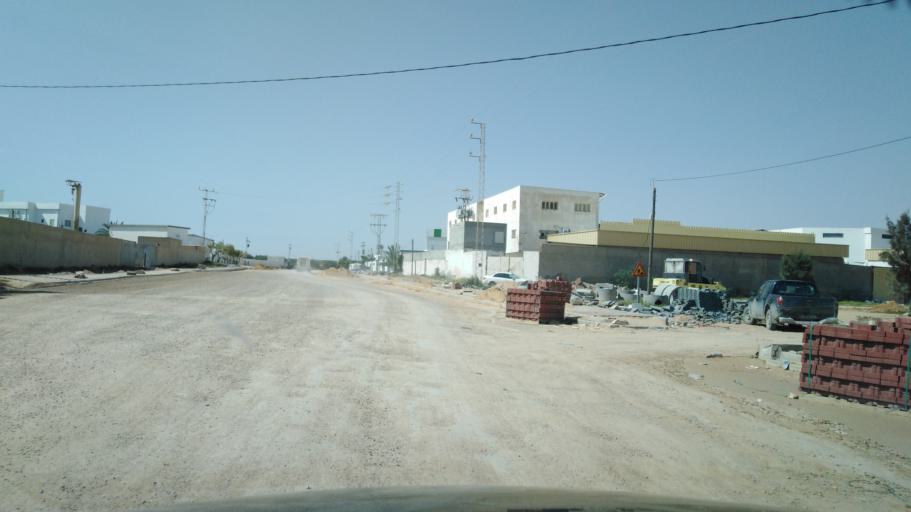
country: TN
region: Safaqis
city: Sfax
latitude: 34.7273
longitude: 10.5142
